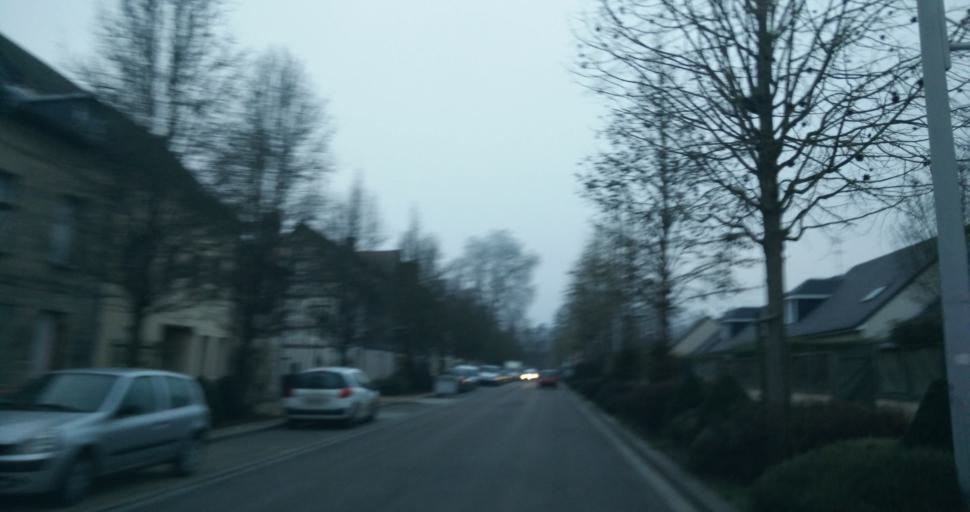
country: FR
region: Haute-Normandie
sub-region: Departement de l'Eure
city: Louviers
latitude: 49.2098
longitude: 1.1779
